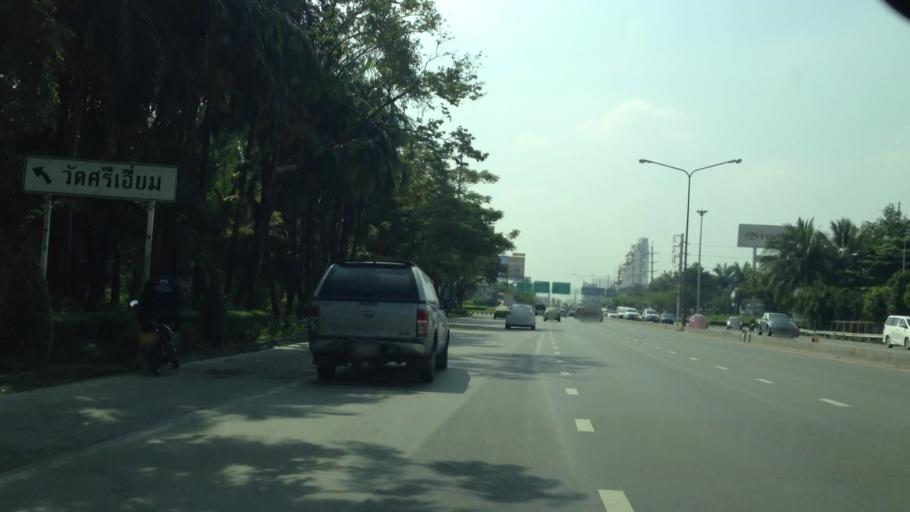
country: TH
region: Bangkok
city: Bang Na
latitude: 13.6632
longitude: 100.6439
